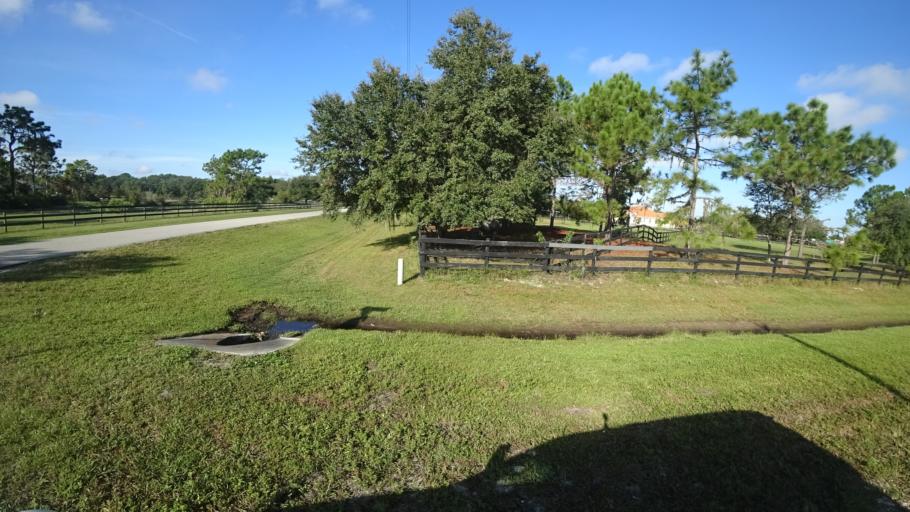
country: US
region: Florida
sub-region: Sarasota County
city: The Meadows
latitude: 27.4168
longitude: -82.3245
